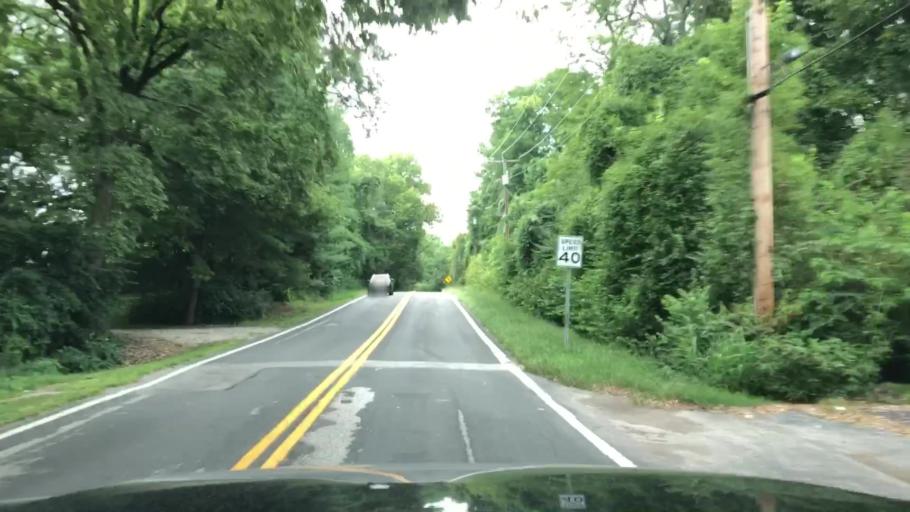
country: US
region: Missouri
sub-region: Saint Louis County
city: Hazelwood
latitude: 38.8145
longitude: -90.3729
